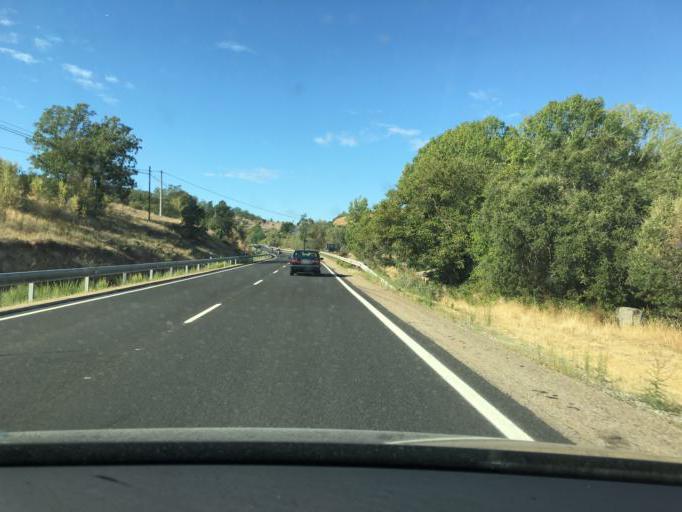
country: ES
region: Madrid
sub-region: Provincia de Madrid
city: Venturada
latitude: 40.8010
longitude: -3.6112
